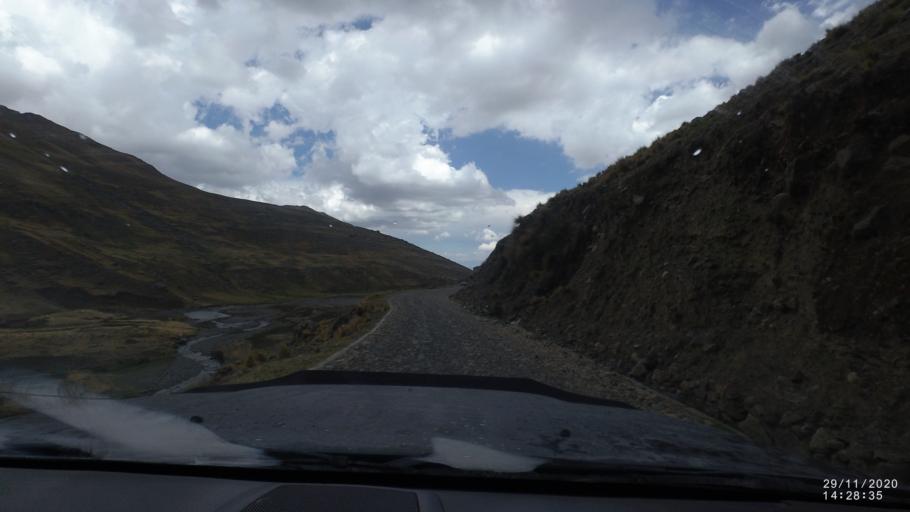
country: BO
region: Cochabamba
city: Sipe Sipe
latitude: -17.2589
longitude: -66.3588
